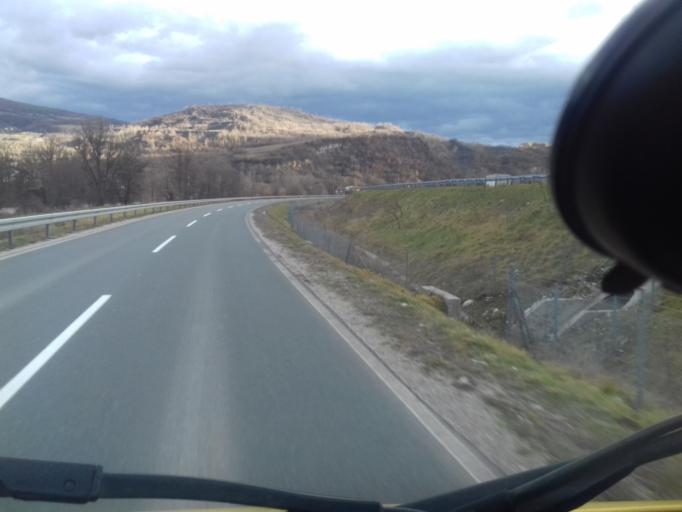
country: BA
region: Federation of Bosnia and Herzegovina
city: Kakanj
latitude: 44.1341
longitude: 18.0715
